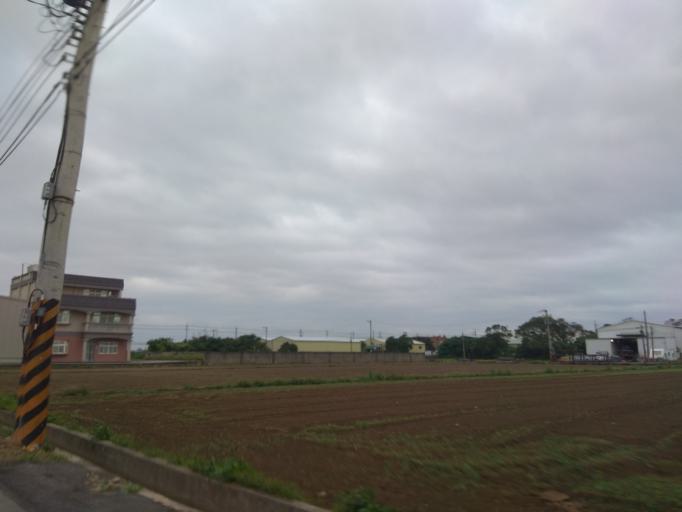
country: TW
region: Taiwan
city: Taoyuan City
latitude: 25.0353
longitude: 121.2190
